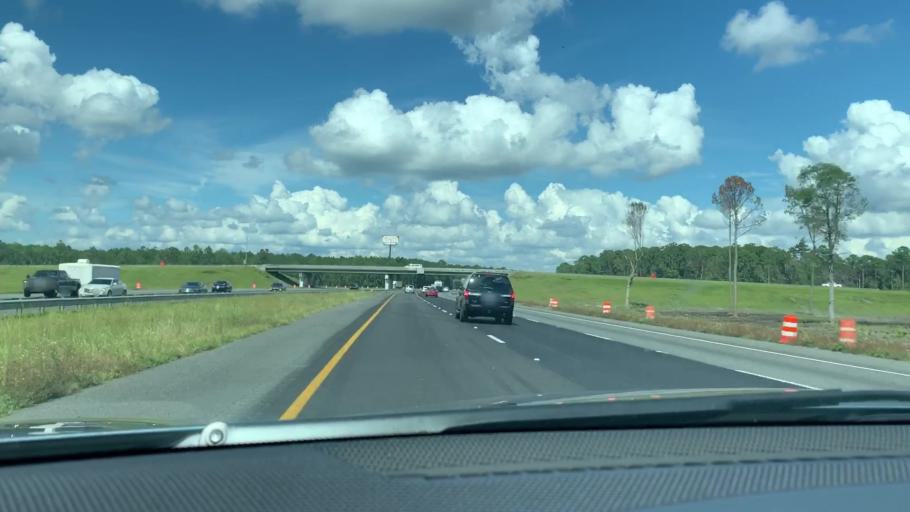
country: US
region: Georgia
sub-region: Camden County
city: Woodbine
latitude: 30.9438
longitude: -81.6863
